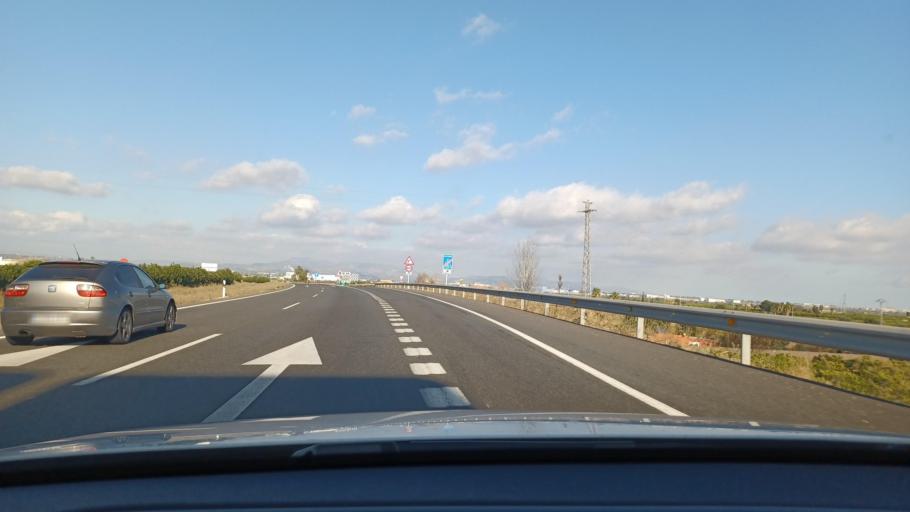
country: ES
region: Valencia
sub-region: Provincia de Castello
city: Betxi
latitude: 39.9238
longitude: -0.1925
